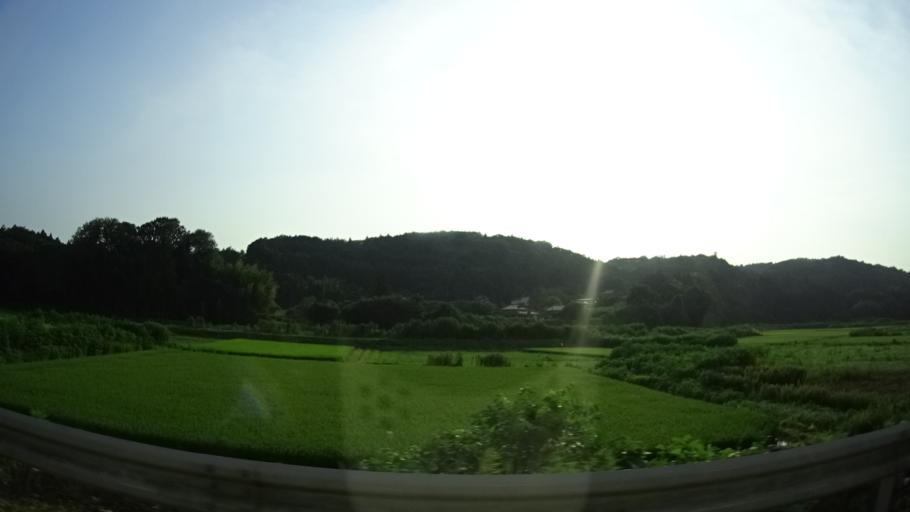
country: JP
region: Tochigi
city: Karasuyama
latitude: 36.6290
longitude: 140.1528
